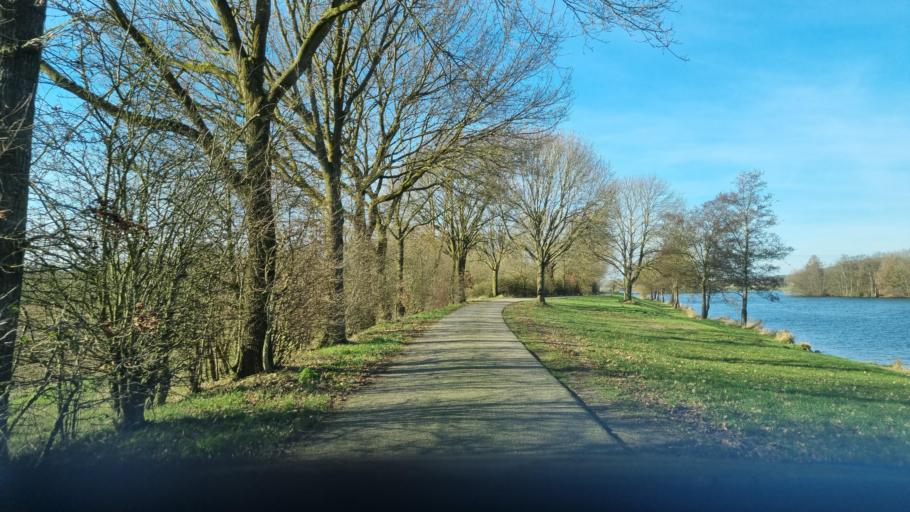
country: NL
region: North Brabant
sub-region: Gemeente Cuijk
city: Cuijk
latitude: 51.7355
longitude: 5.9071
